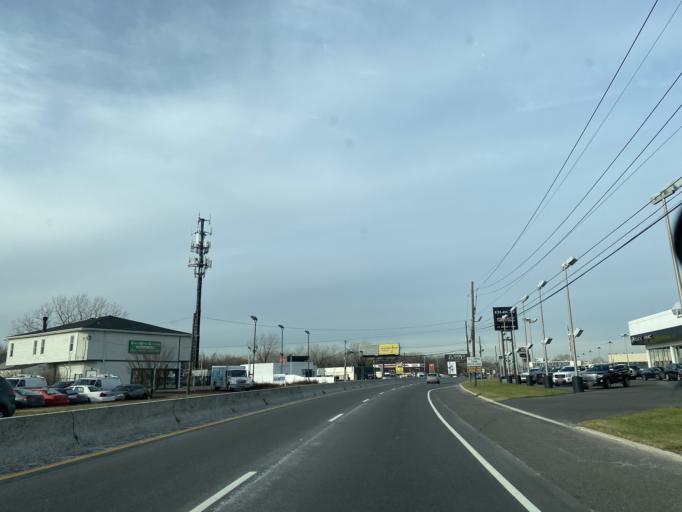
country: US
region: New Jersey
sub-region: Burlington County
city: Palmyra
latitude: 39.9986
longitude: -75.0352
